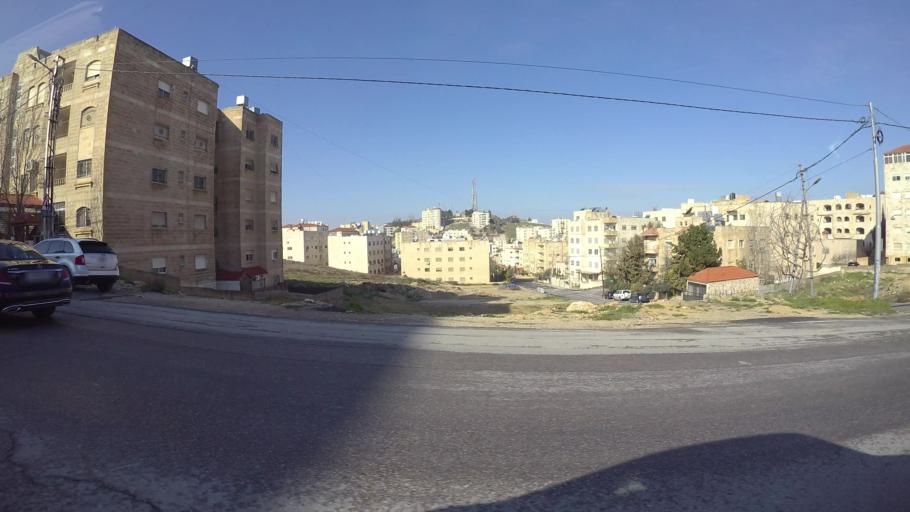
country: JO
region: Amman
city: Al Jubayhah
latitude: 32.0069
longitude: 35.8507
